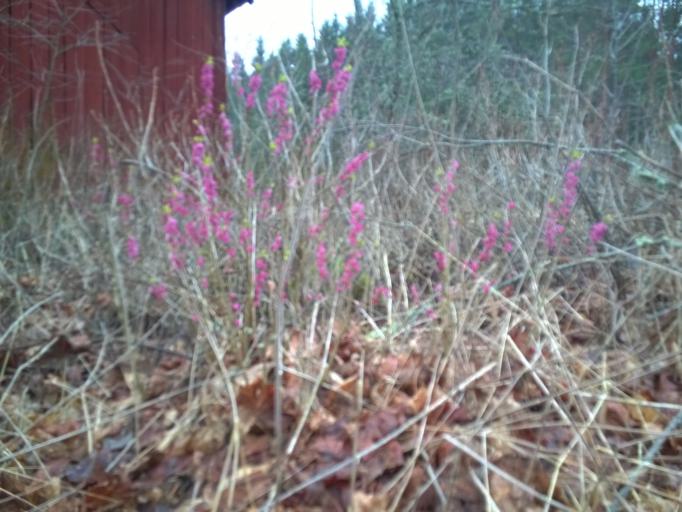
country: SE
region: Uppsala
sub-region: Osthammars Kommun
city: Bjorklinge
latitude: 60.1587
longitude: 17.5066
